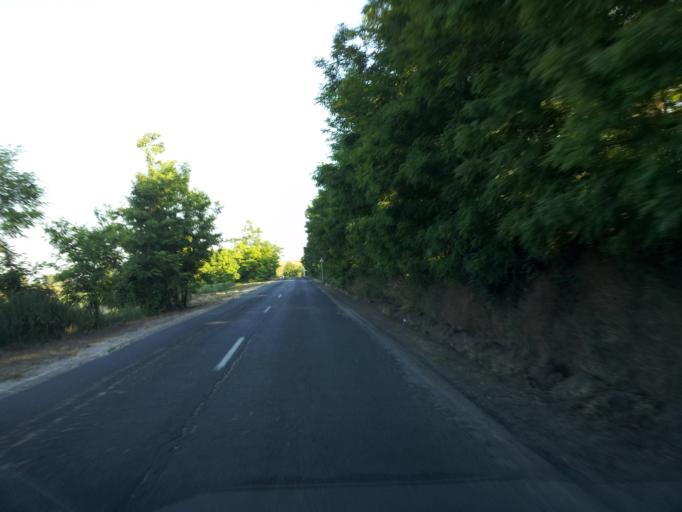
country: HU
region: Fejer
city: Bicske
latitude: 47.5128
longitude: 18.6235
